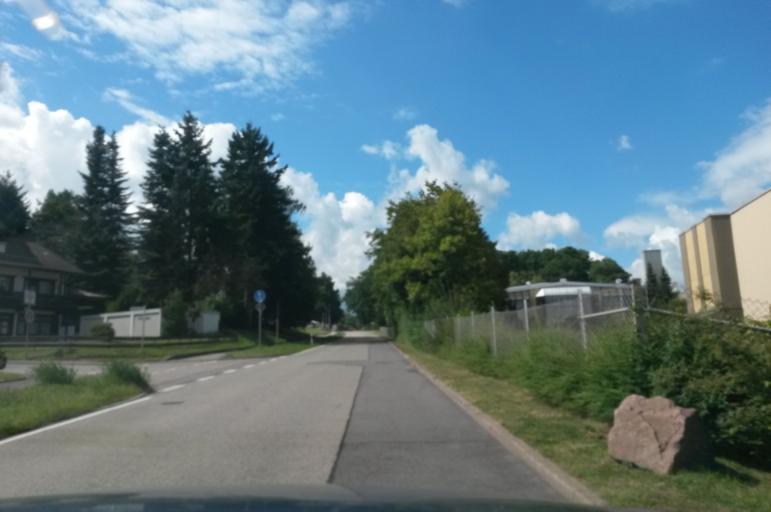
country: DE
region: Baden-Wuerttemberg
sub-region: Karlsruhe Region
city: Dobel
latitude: 48.8472
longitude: 8.5190
